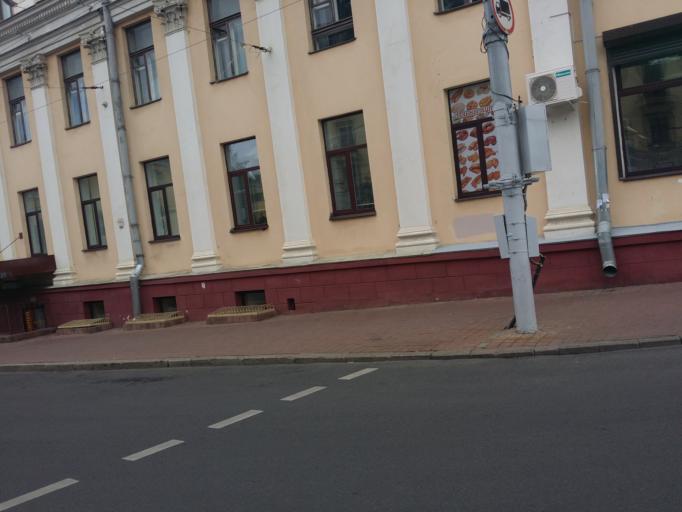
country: BY
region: Minsk
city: Minsk
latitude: 53.9137
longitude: 27.5753
